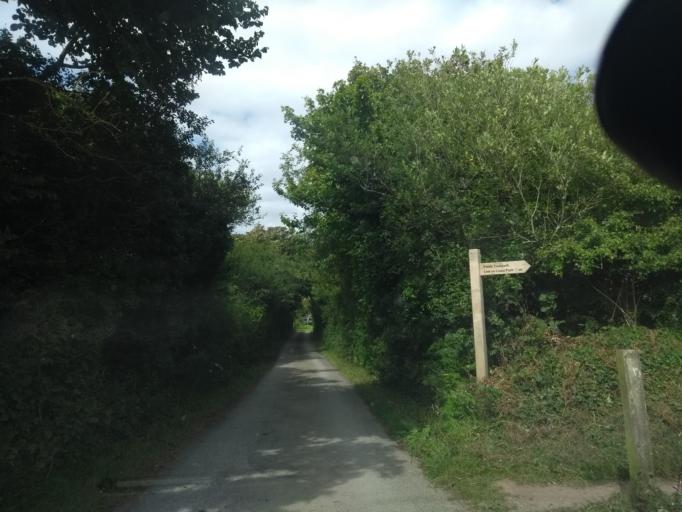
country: GB
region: England
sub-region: Devon
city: Modbury
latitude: 50.2949
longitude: -3.8966
